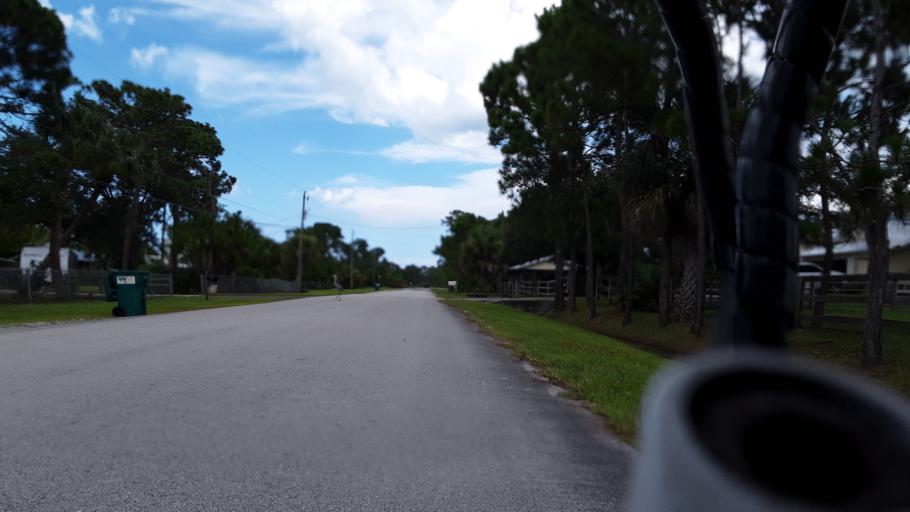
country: US
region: Florida
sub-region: Brevard County
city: Malabar
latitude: 27.9834
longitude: -80.5792
